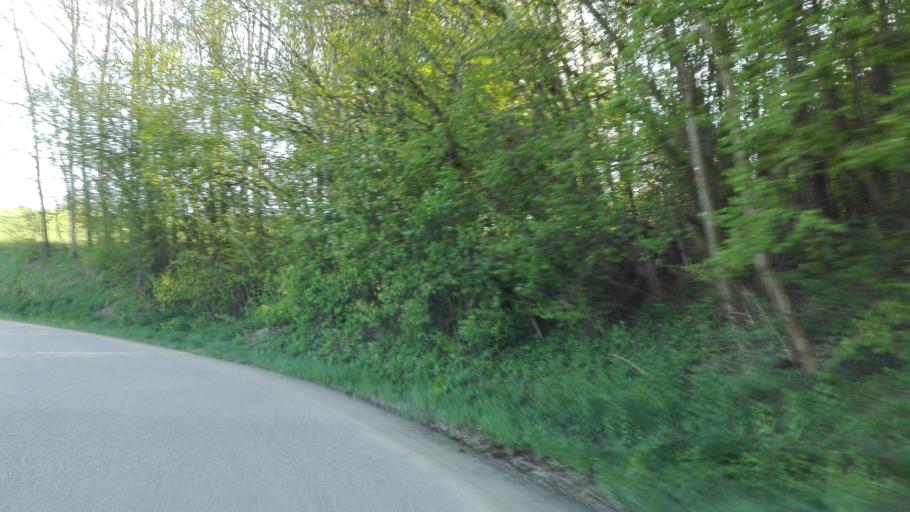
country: AT
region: Upper Austria
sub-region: Politischer Bezirk Grieskirchen
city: Grieskirchen
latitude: 48.3624
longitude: 13.7848
